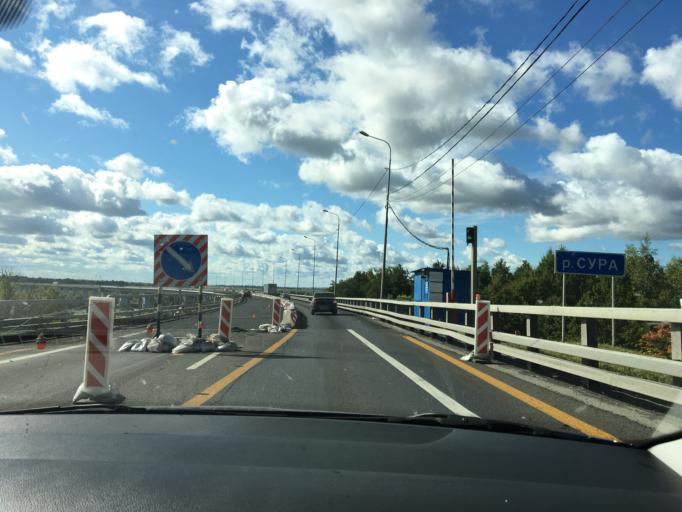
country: RU
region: Chuvashia
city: Yadrin
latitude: 56.0338
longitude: 46.2440
